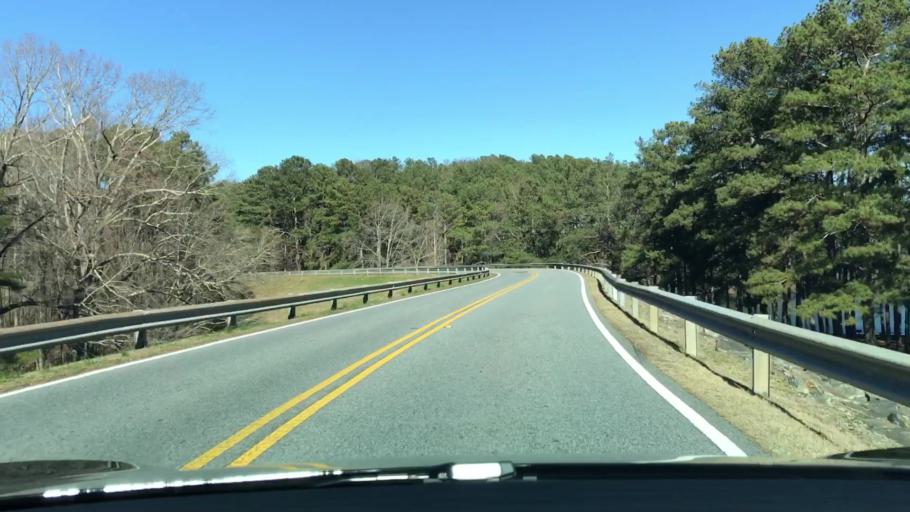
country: US
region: Georgia
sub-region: Forsyth County
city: Cumming
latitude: 34.1722
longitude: -84.0782
